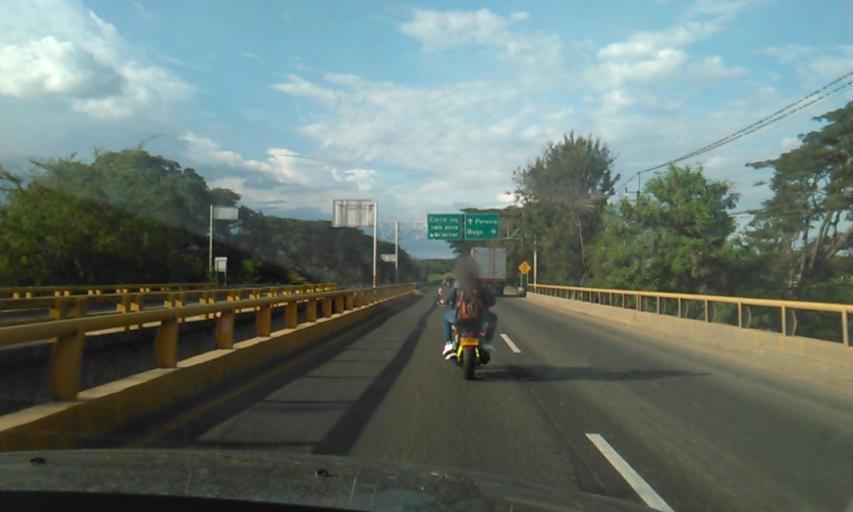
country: CO
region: Valle del Cauca
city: Buga
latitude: 3.8971
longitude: -76.3126
